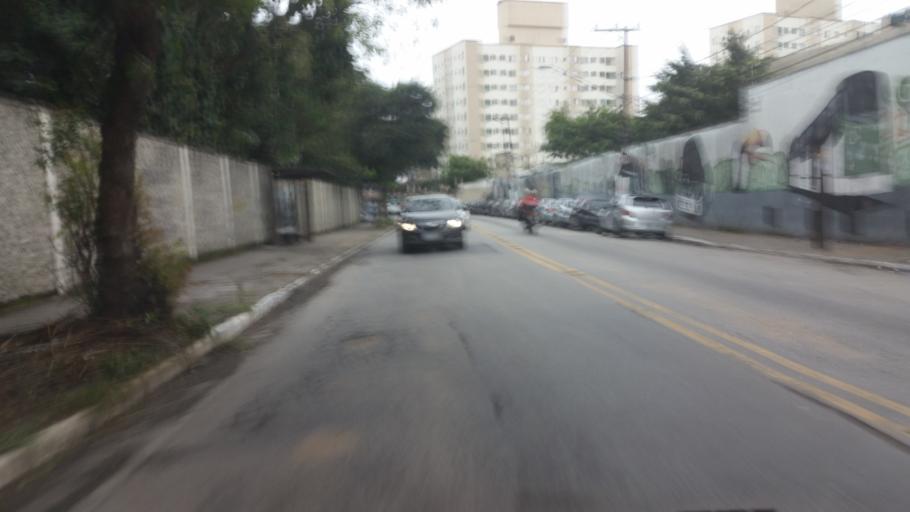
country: BR
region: Sao Paulo
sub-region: Diadema
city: Diadema
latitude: -23.6509
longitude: -46.6143
